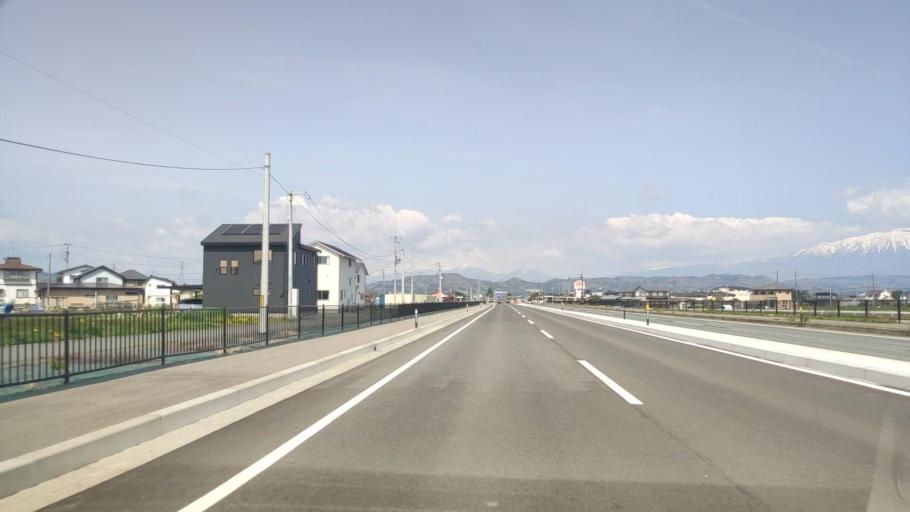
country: JP
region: Iwate
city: Morioka-shi
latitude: 39.6873
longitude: 141.1148
